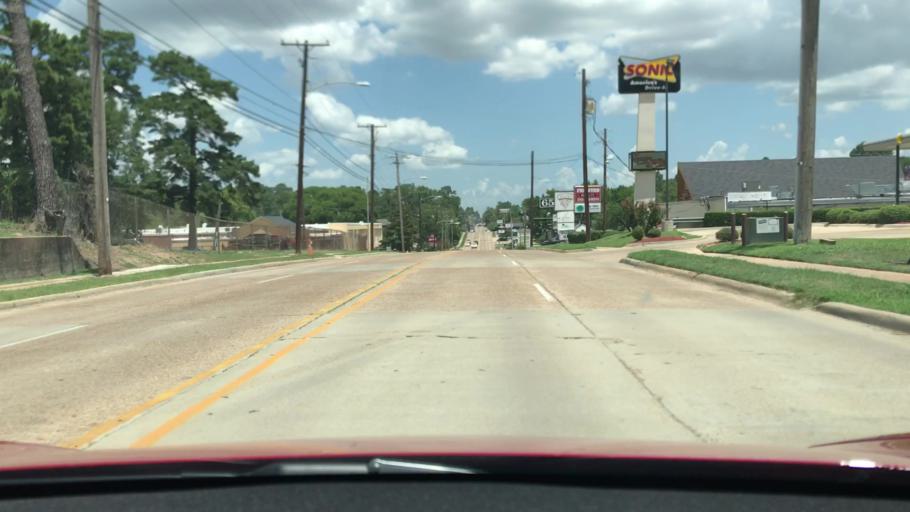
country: US
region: Louisiana
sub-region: Bossier Parish
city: Bossier City
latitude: 32.4452
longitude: -93.7459
